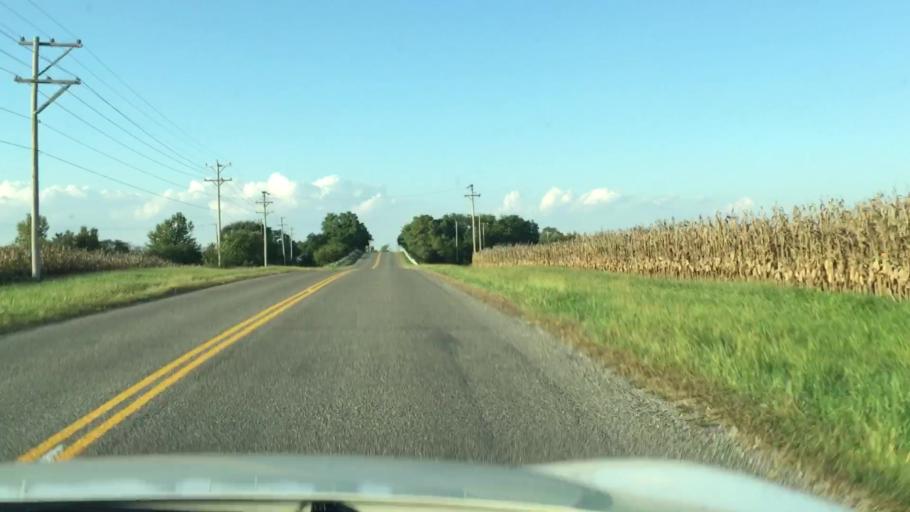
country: US
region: Ohio
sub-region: Champaign County
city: Urbana
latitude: 40.0944
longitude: -83.7715
